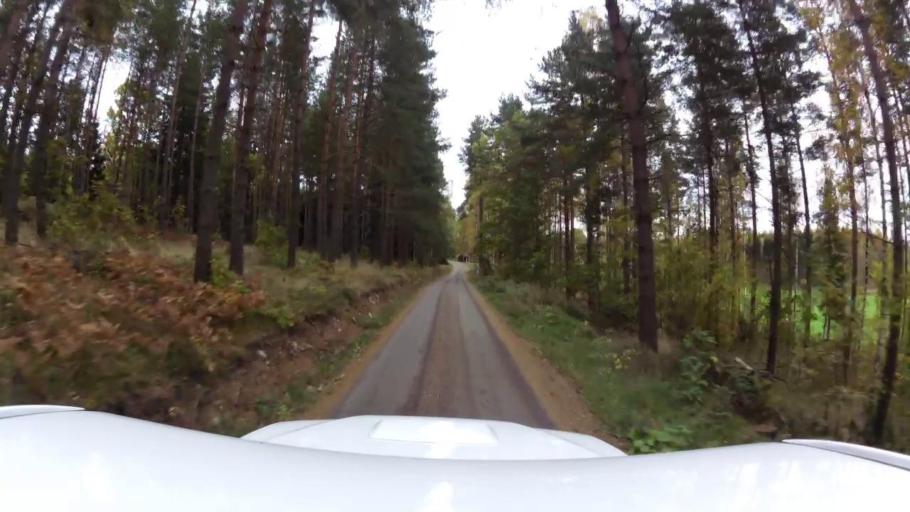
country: SE
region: OEstergoetland
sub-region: Linkopings Kommun
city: Ljungsbro
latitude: 58.5437
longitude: 15.4404
